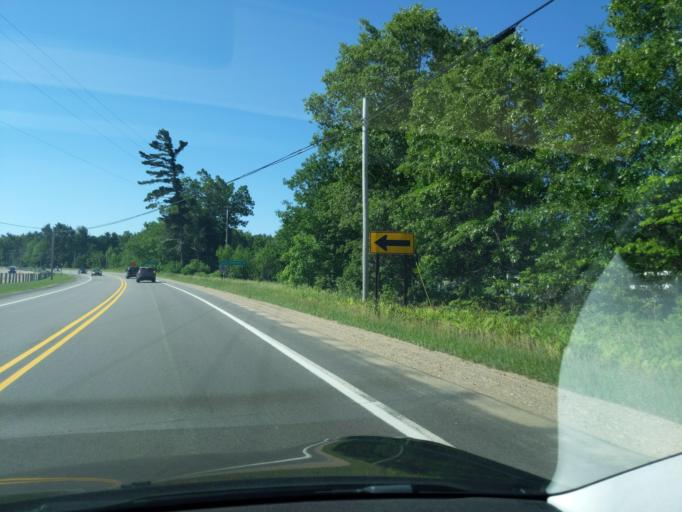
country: US
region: Michigan
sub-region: Muskegon County
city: Lakewood Club
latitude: 43.3430
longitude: -86.2819
